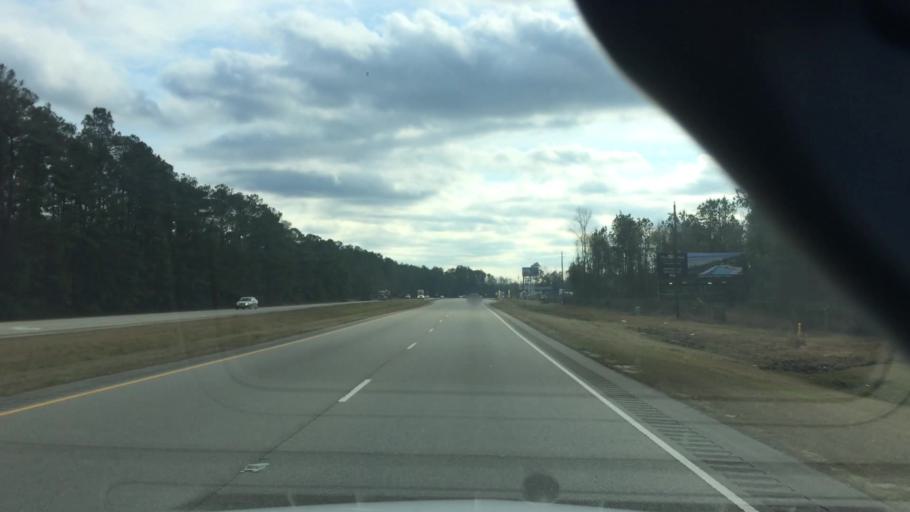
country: US
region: North Carolina
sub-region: Brunswick County
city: Bolivia
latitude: 34.1444
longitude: -78.0939
